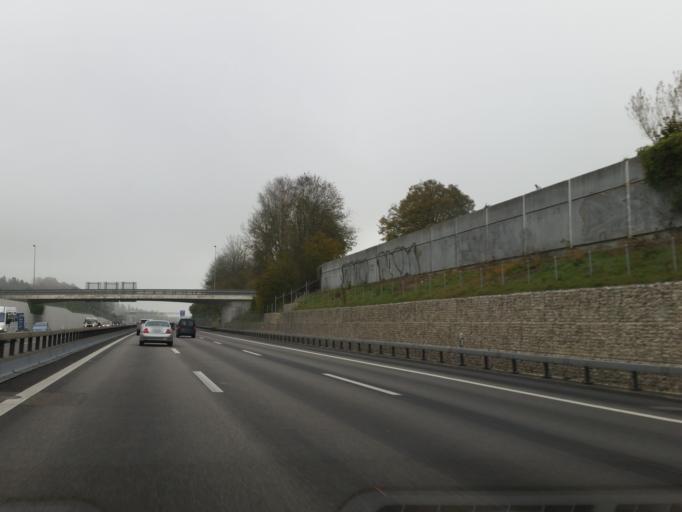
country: CH
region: Solothurn
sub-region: Bezirk Olten
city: Gunzgen
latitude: 47.3114
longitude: 7.8224
